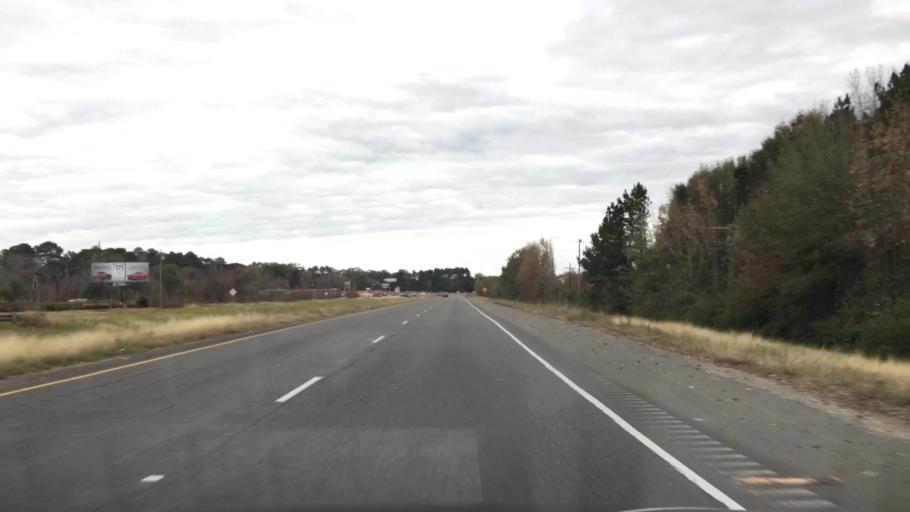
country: US
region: Louisiana
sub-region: Vernon Parish
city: New Llano
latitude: 31.1072
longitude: -93.2708
